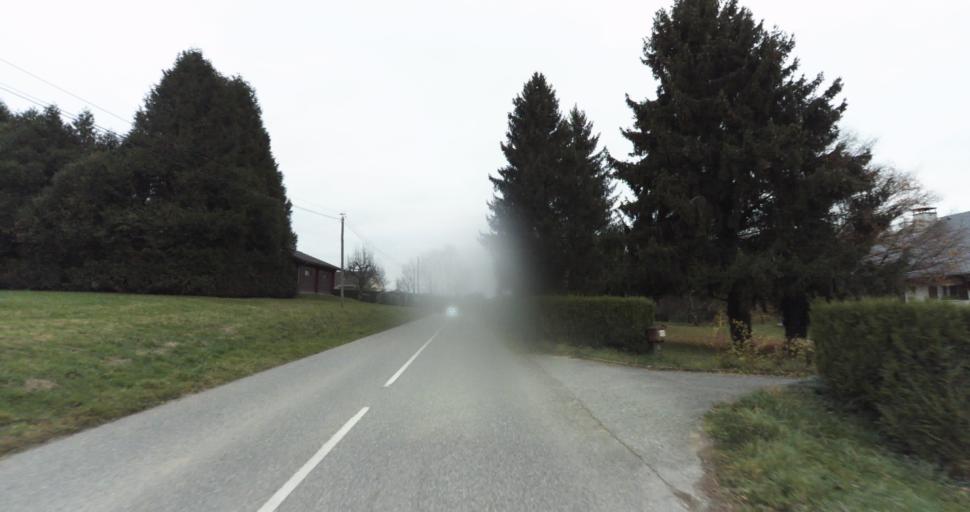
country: FR
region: Rhone-Alpes
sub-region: Departement de la Haute-Savoie
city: Saint-Felix
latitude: 45.8195
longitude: 5.9749
